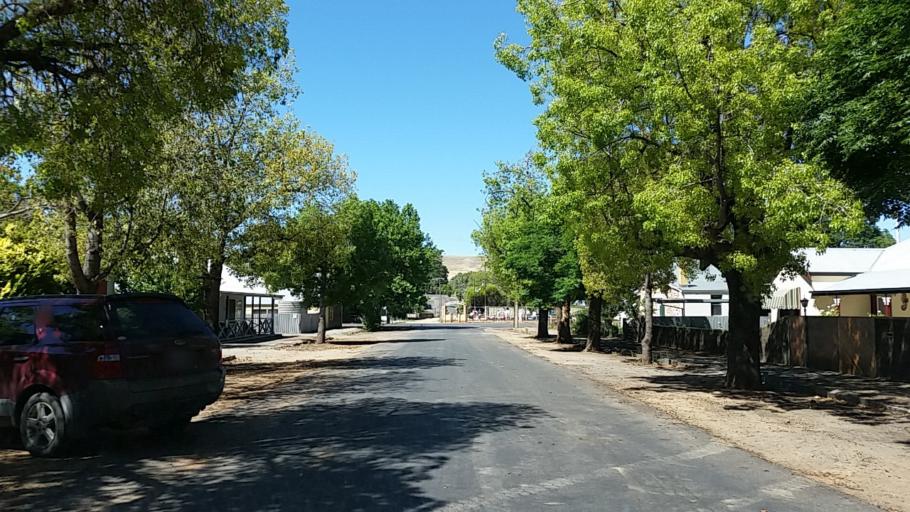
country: AU
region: South Australia
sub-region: Clare and Gilbert Valleys
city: Clare
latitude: -33.6836
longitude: 138.9395
